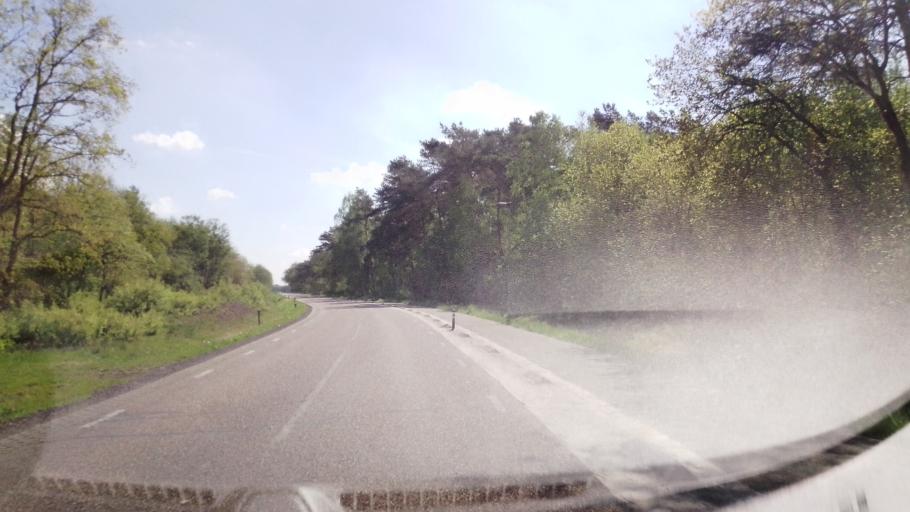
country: NL
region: Limburg
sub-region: Gemeente Venray
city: Venray
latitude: 51.4497
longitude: 5.9775
